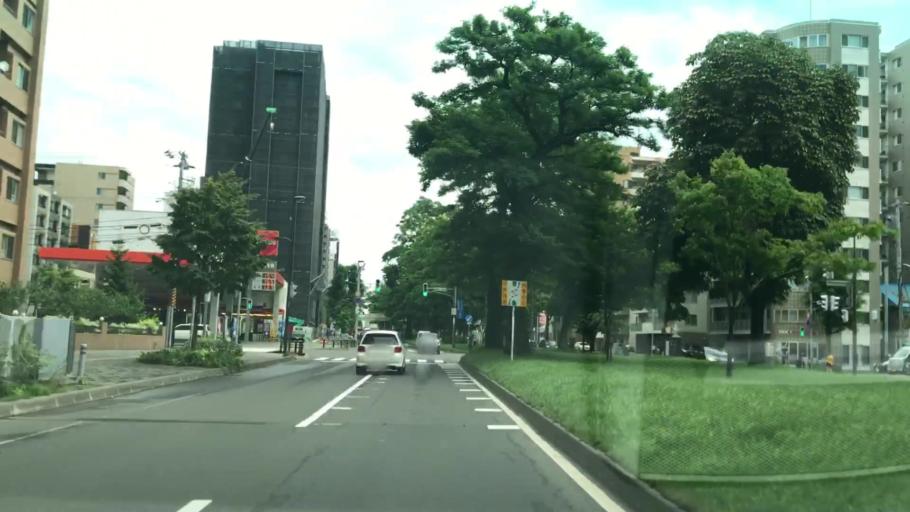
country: JP
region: Hokkaido
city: Sapporo
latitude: 43.0546
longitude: 141.3448
